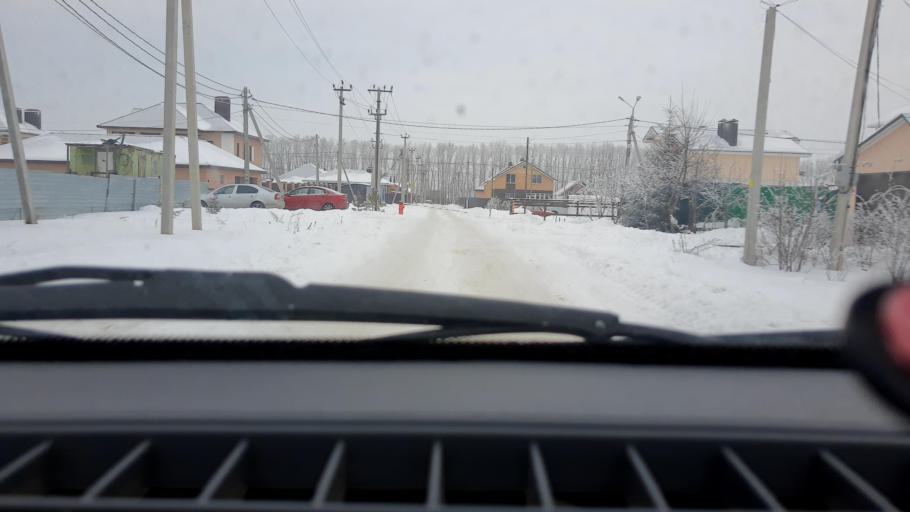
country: RU
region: Bashkortostan
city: Kabakovo
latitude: 54.6335
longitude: 56.1083
